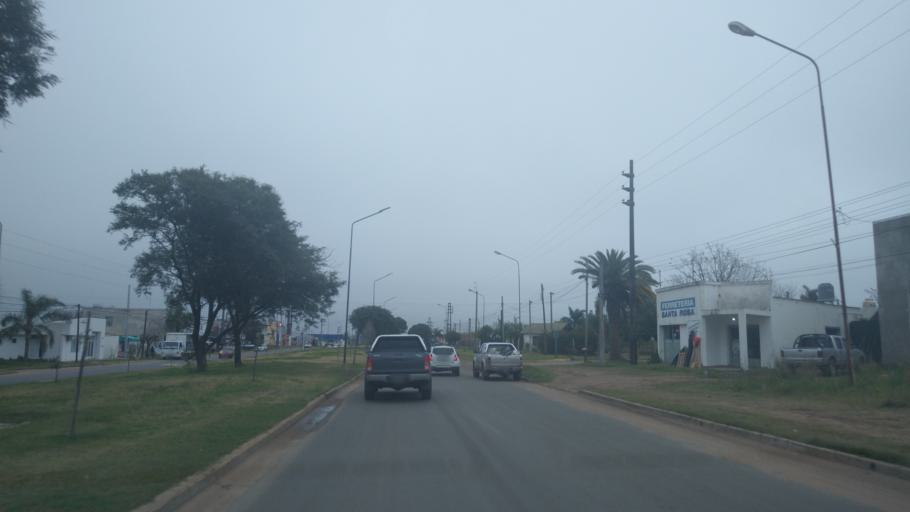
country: AR
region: Entre Rios
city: Chajari
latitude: -30.7614
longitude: -58.0072
